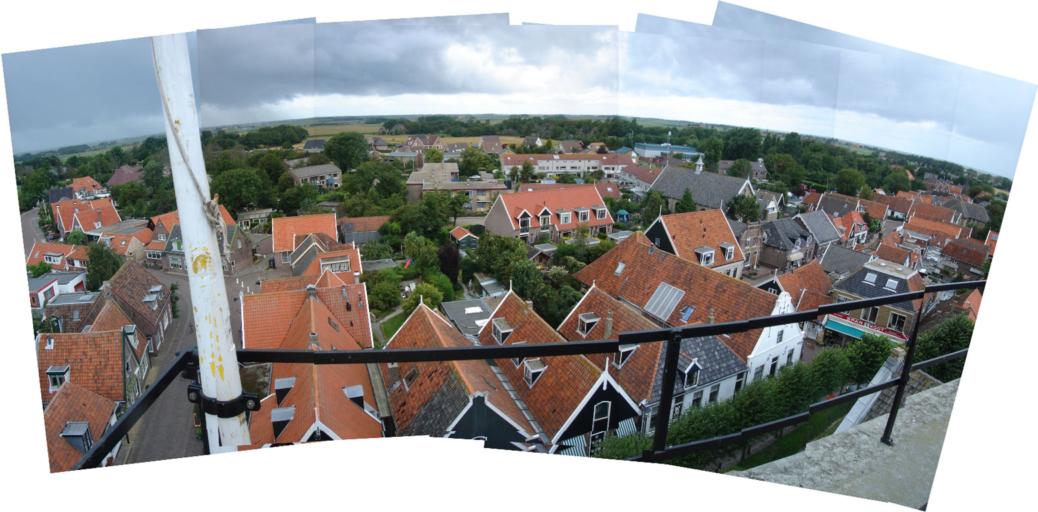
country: NL
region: North Holland
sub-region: Gemeente Texel
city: Den Burg
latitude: 53.0841
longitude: 4.8731
